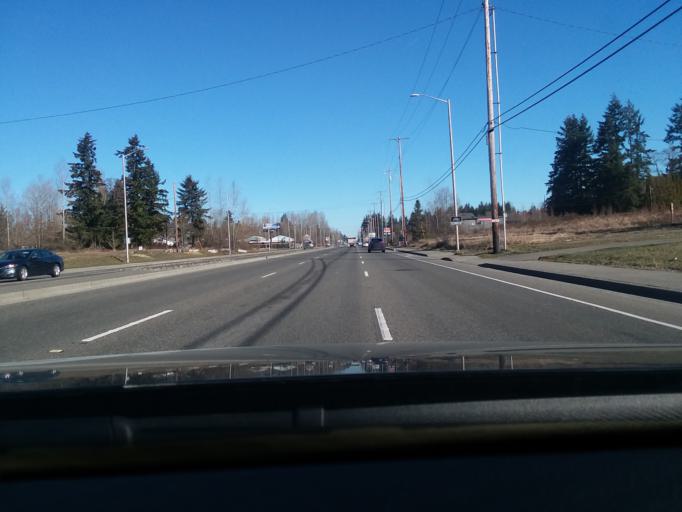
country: US
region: Washington
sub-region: Pierce County
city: Summit
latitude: 47.1341
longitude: -122.3573
